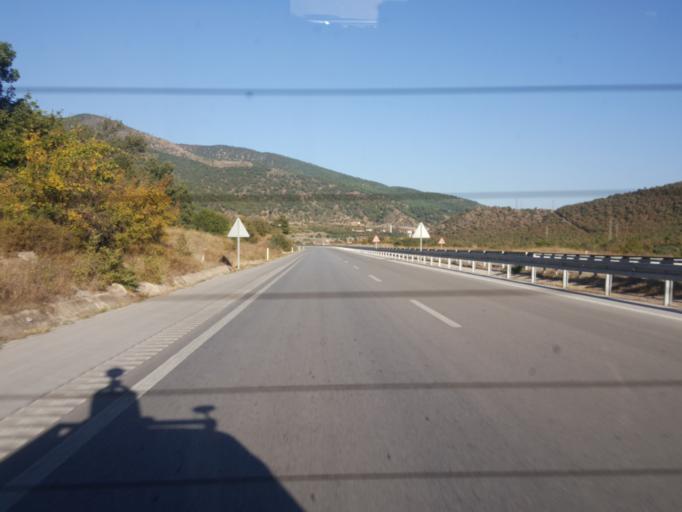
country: TR
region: Amasya
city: Tekke
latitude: 40.7472
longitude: 36.1298
